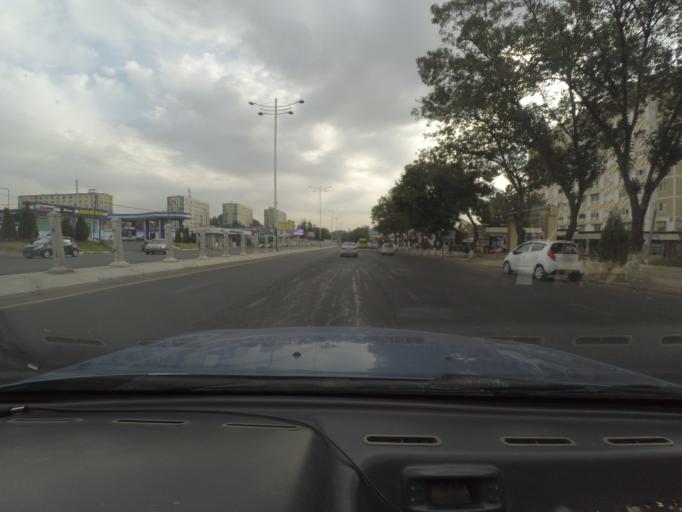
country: UZ
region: Toshkent
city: Salor
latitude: 41.3581
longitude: 69.3840
